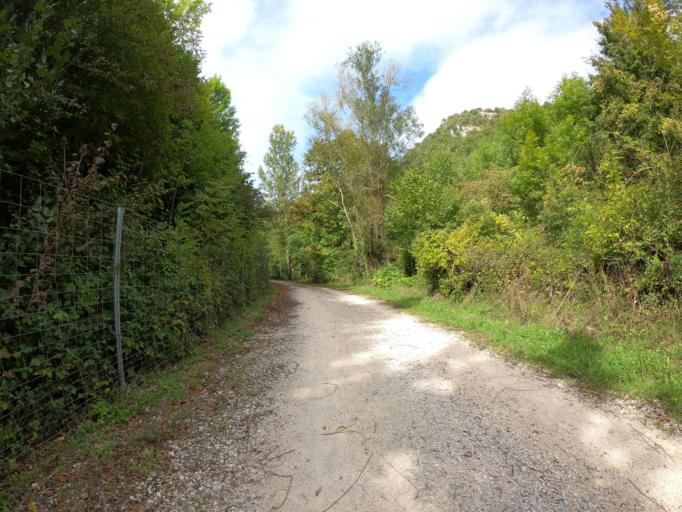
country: ES
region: Navarre
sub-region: Provincia de Navarra
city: Irurtzun
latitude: 42.9421
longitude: -1.8237
